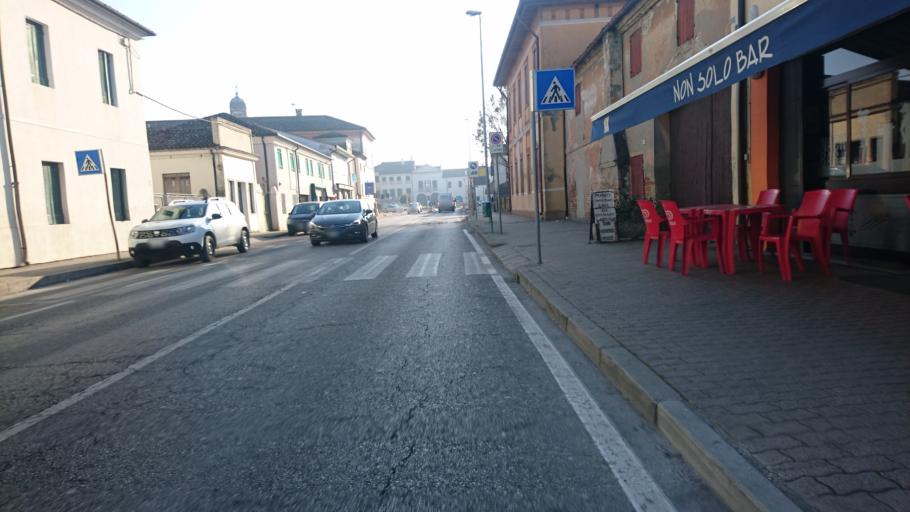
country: IT
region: Veneto
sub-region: Provincia di Padova
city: Bagnoli di Sopra
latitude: 45.1859
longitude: 11.8842
